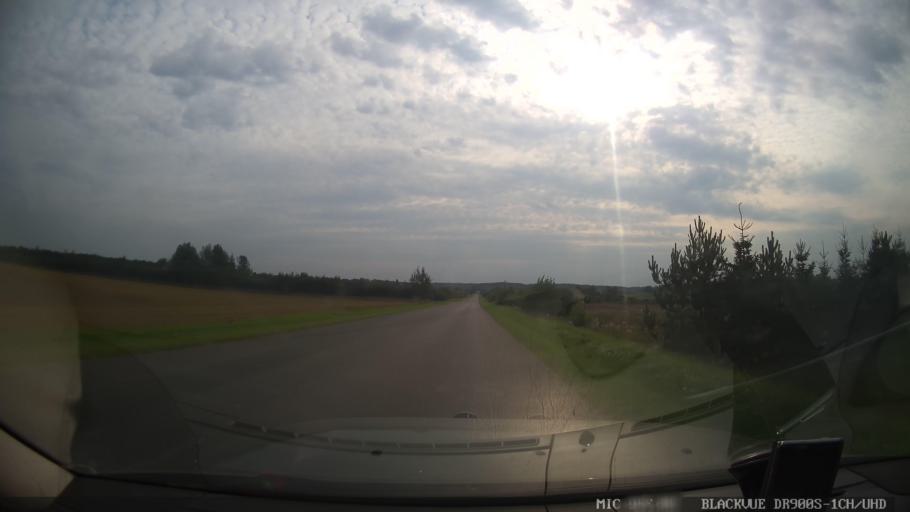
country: LT
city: Skaidiskes
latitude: 54.5519
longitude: 25.6592
